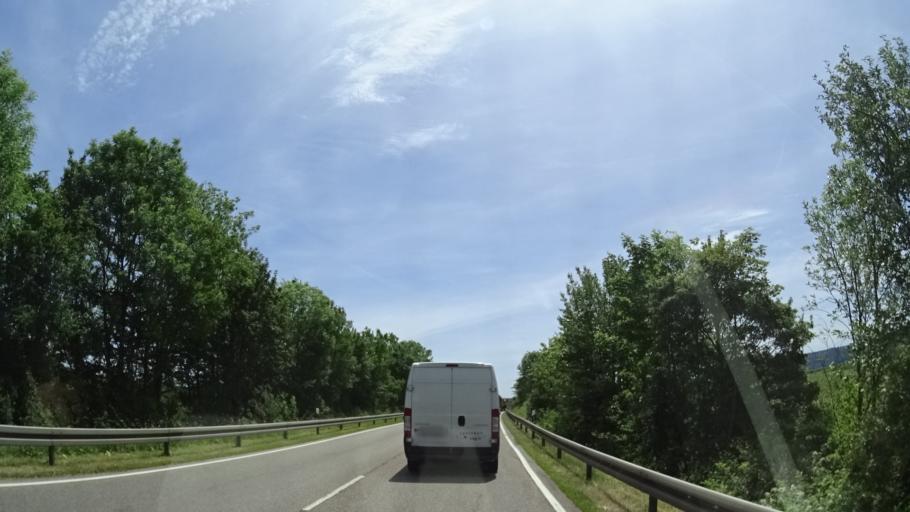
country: DE
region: Baden-Wuerttemberg
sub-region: Regierungsbezirk Stuttgart
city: Untermunkheim
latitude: 49.1720
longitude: 9.7131
